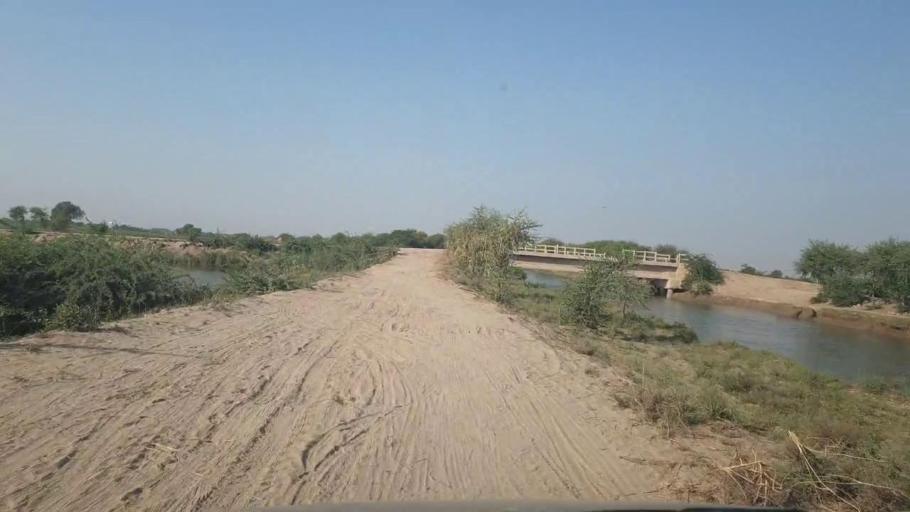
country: PK
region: Sindh
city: Badin
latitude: 24.6386
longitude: 68.8150
